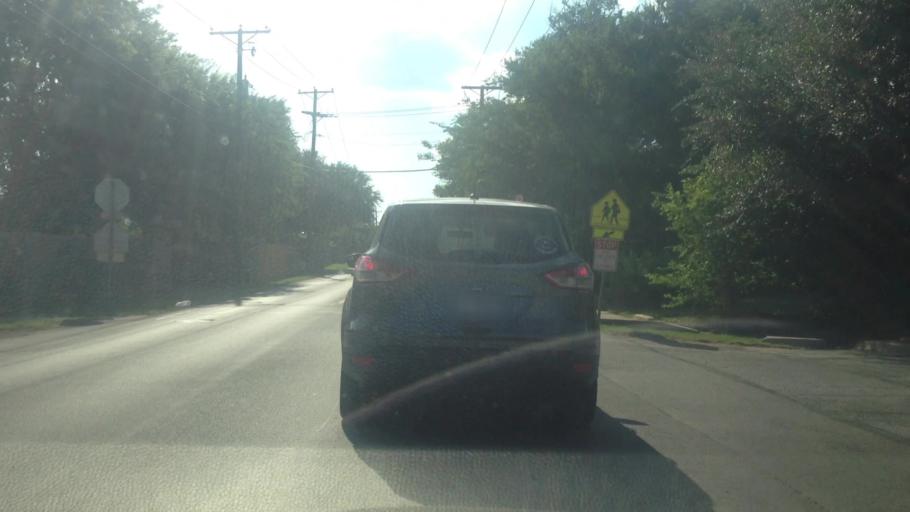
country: US
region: Texas
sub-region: Tarrant County
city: Watauga
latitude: 32.8677
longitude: -97.2488
